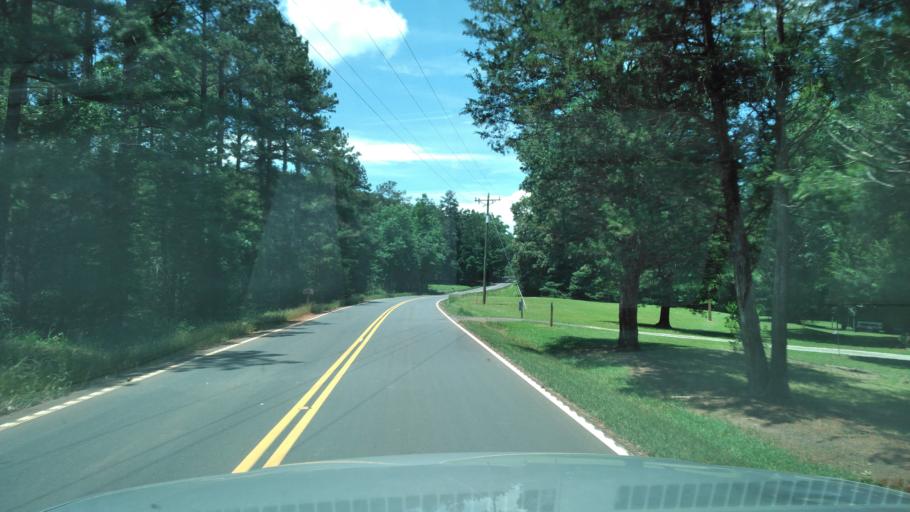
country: US
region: South Carolina
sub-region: Greenwood County
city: Ware Shoals
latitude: 34.4248
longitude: -82.1329
